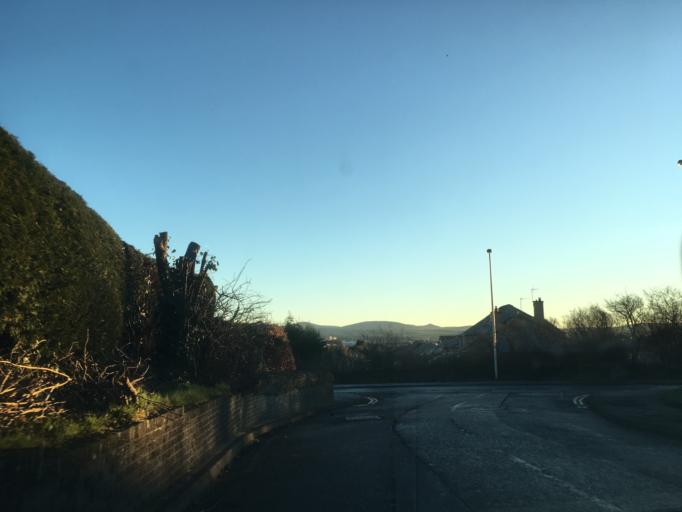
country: GB
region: Scotland
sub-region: Edinburgh
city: Currie
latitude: 55.9457
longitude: -3.3011
